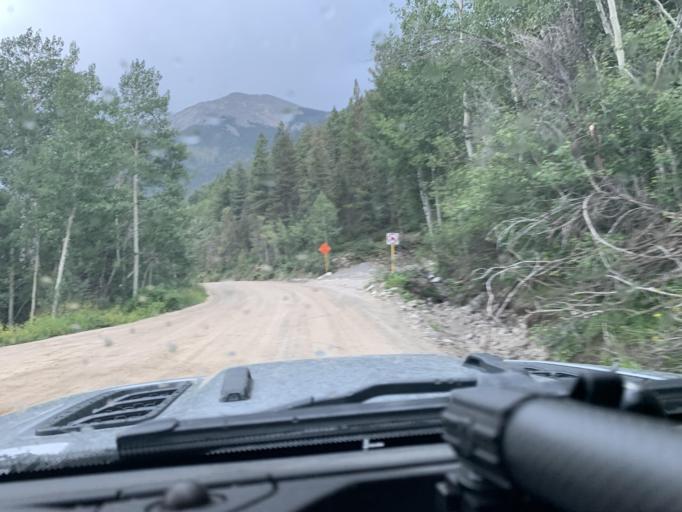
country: US
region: Colorado
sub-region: Chaffee County
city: Buena Vista
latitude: 38.7097
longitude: -106.2893
